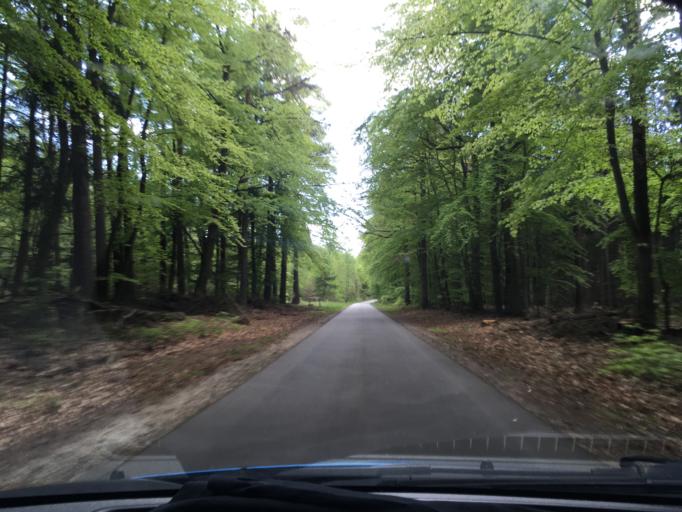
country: DE
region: Lower Saxony
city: Nahrendorf
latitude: 53.1379
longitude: 10.8018
